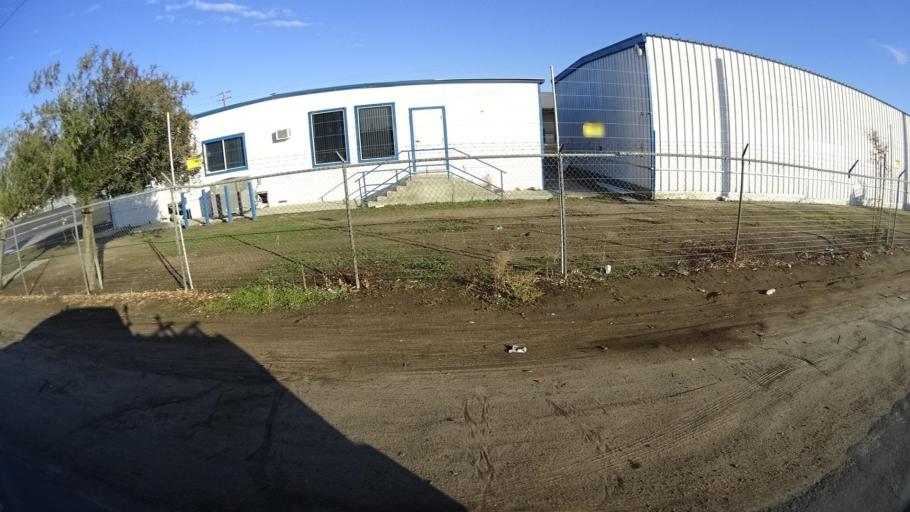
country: US
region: California
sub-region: Kern County
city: Delano
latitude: 35.7905
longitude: -119.2543
